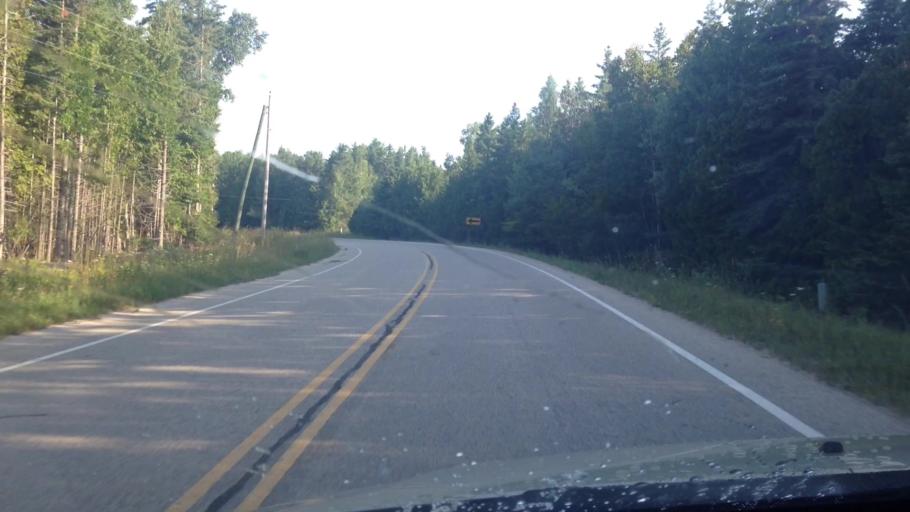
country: US
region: Michigan
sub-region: Mackinac County
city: Saint Ignace
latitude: 45.8914
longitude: -84.7659
